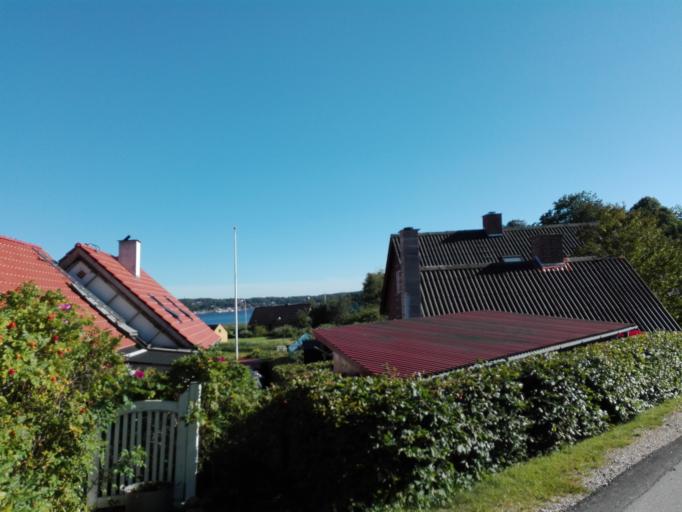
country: DK
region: North Denmark
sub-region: Mariagerfjord Kommune
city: Mariager
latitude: 56.6727
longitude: 9.9690
